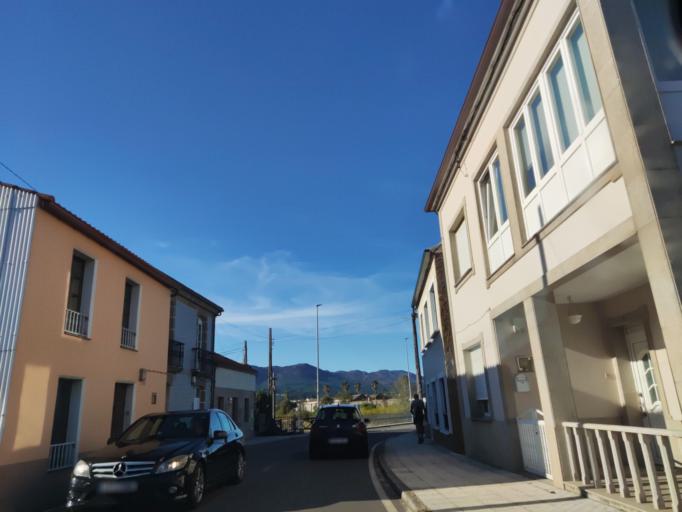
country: ES
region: Galicia
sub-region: Provincia da Coruna
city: Boiro
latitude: 42.5967
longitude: -8.9337
